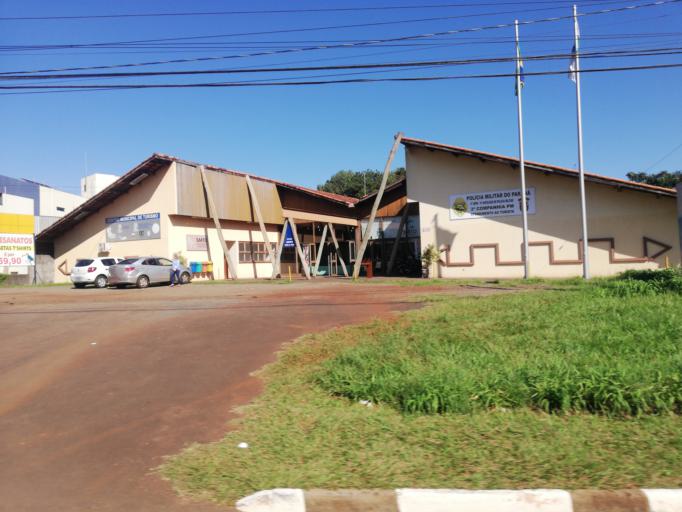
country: BR
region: Parana
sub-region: Foz Do Iguacu
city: Foz do Iguacu
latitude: -25.5603
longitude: -54.5621
